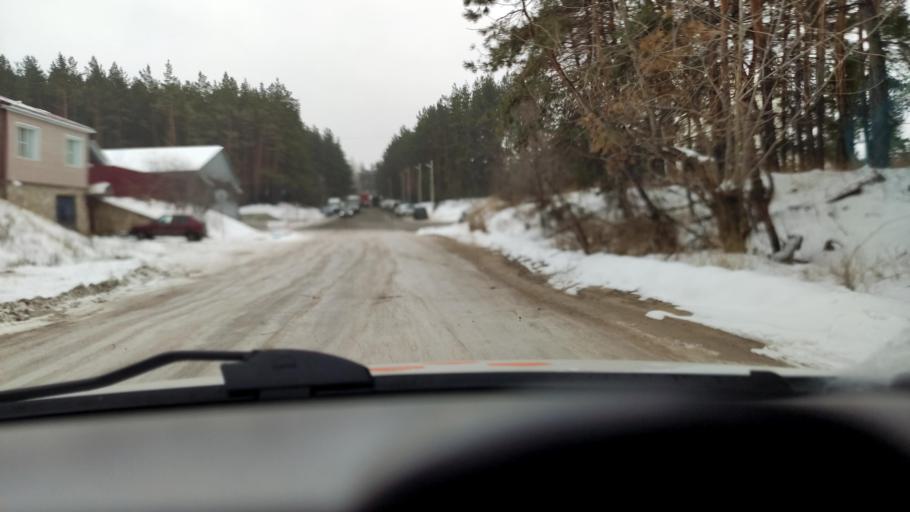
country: RU
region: Voronezj
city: Pridonskoy
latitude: 51.6771
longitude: 39.0819
